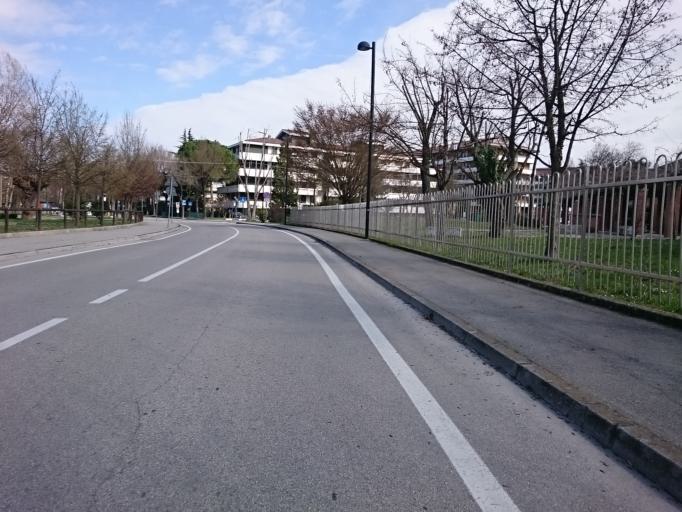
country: IT
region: Veneto
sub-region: Provincia di Padova
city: Mandriola-Sant'Agostino
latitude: 45.3759
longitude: 11.8569
